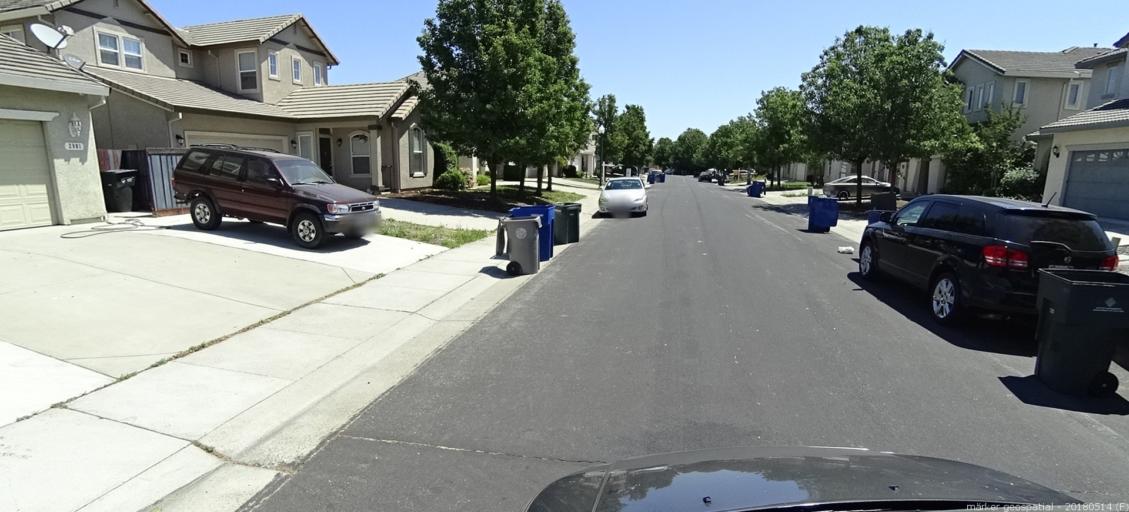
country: US
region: California
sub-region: Yolo County
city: West Sacramento
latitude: 38.6283
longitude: -121.5281
